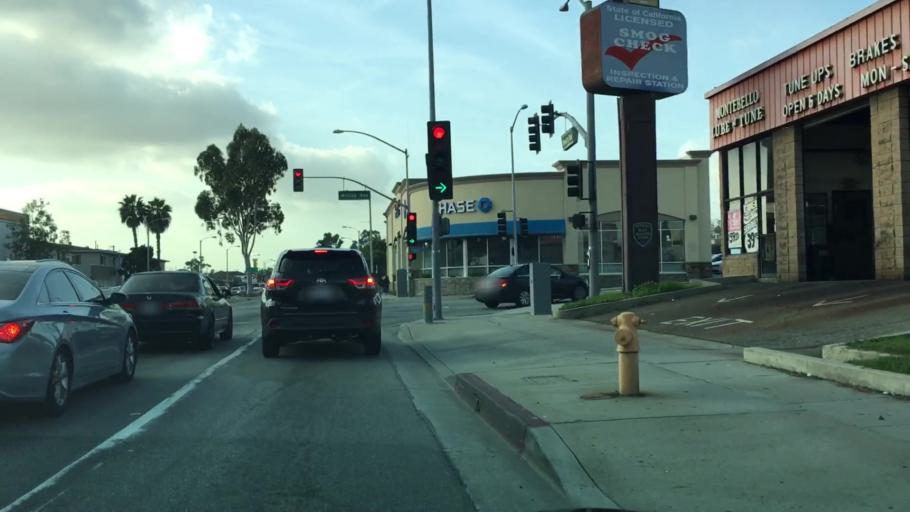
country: US
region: California
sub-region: Los Angeles County
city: Montebello
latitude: 34.0208
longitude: -118.1225
